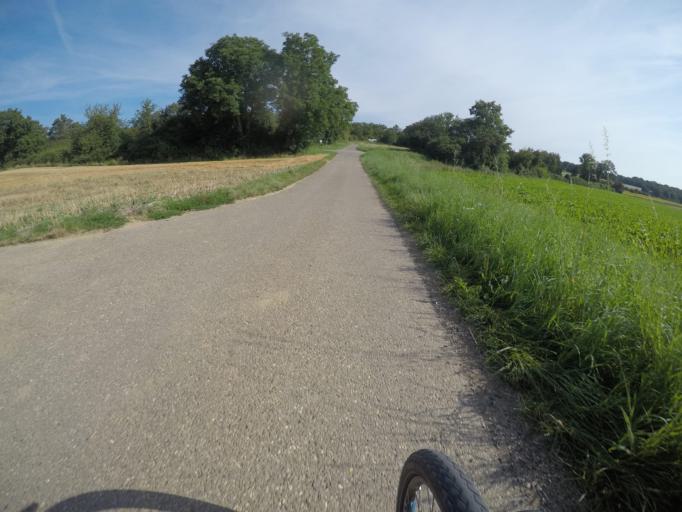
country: DE
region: Baden-Wuerttemberg
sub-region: Regierungsbezirk Stuttgart
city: Weissach
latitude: 48.8529
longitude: 8.9395
